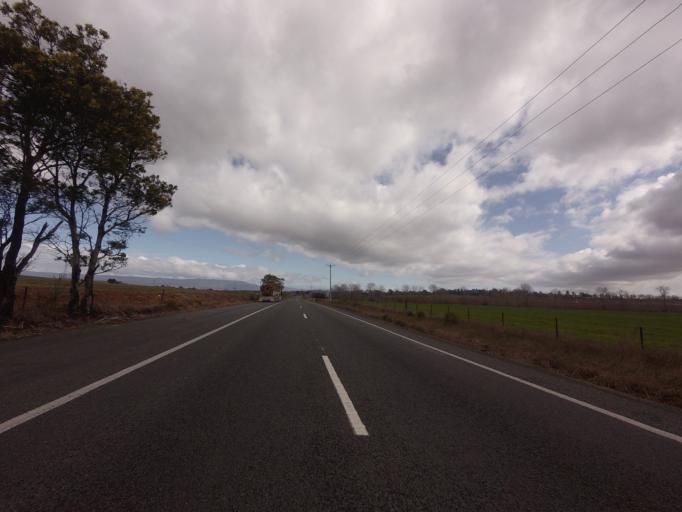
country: AU
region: Tasmania
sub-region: Northern Midlands
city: Evandale
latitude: -41.8352
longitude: 147.4542
